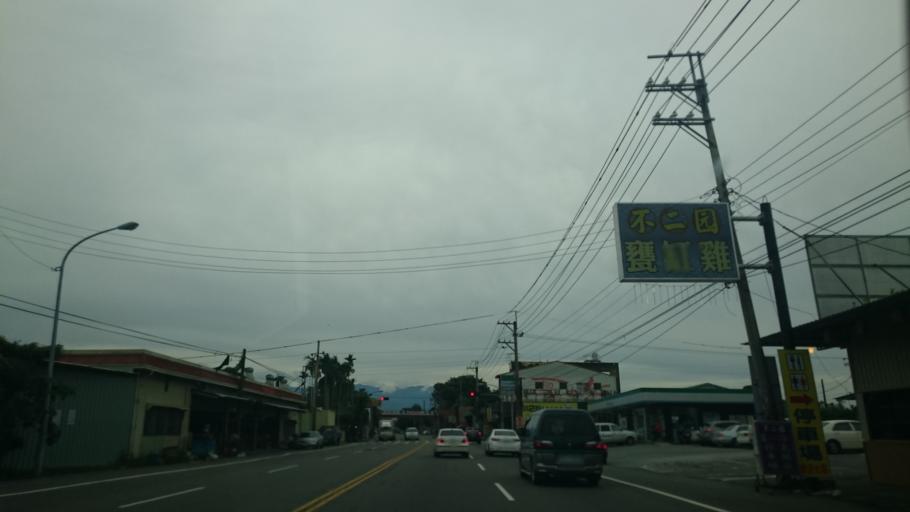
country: TW
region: Taiwan
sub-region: Nantou
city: Nantou
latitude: 23.8474
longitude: 120.6974
